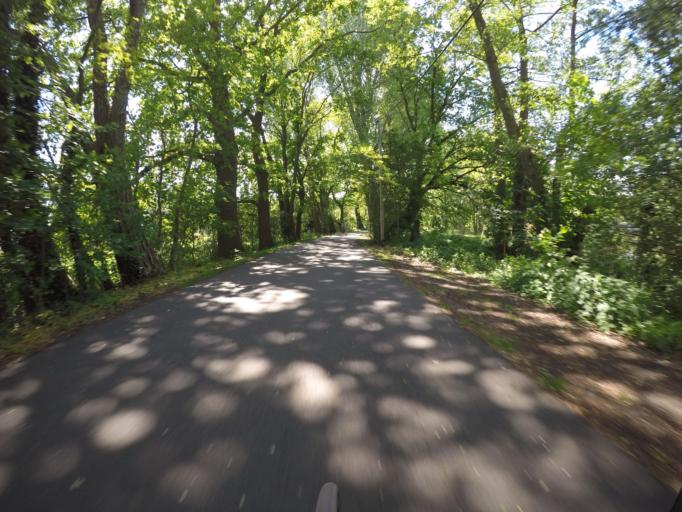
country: DE
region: Brandenburg
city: Werder
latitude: 52.4288
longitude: 12.9533
